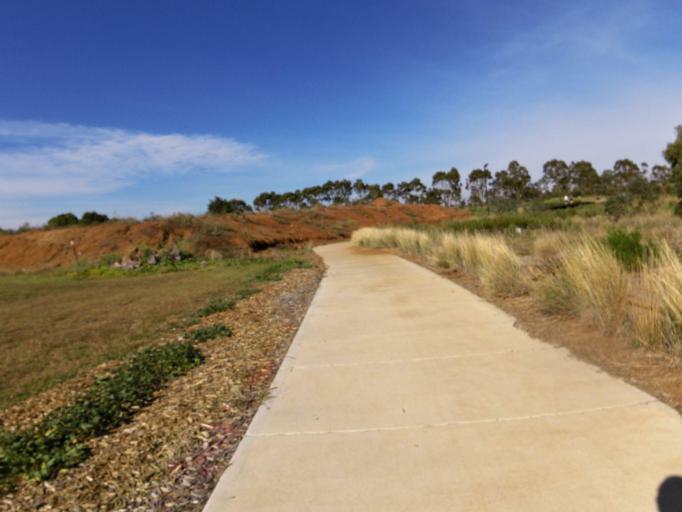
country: AU
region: Victoria
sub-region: Melton
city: Melton
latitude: -37.6929
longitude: 144.5894
